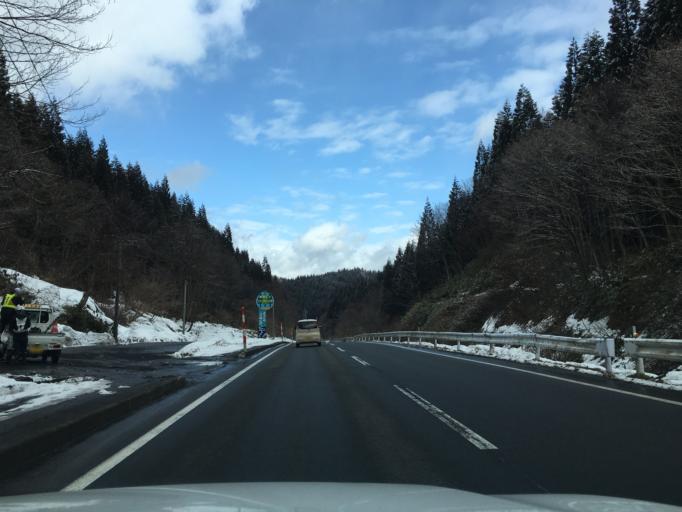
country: JP
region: Akita
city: Takanosu
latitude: 39.9865
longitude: 140.2464
